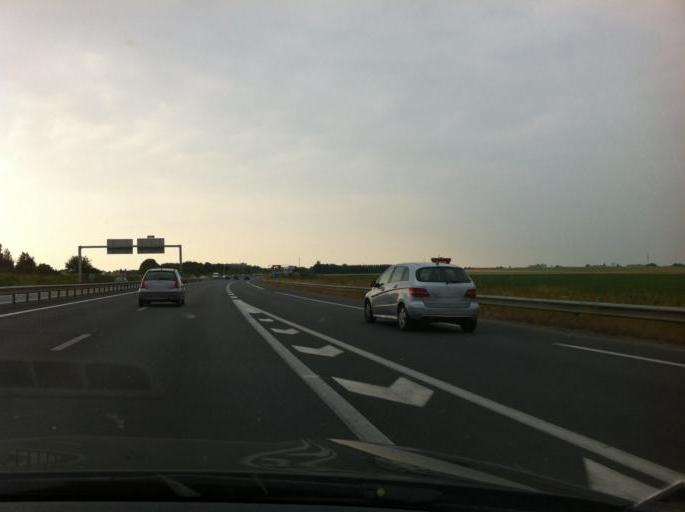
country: FR
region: Ile-de-France
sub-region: Departement de Seine-et-Marne
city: Vert-Saint-Denis
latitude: 48.5746
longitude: 2.6395
